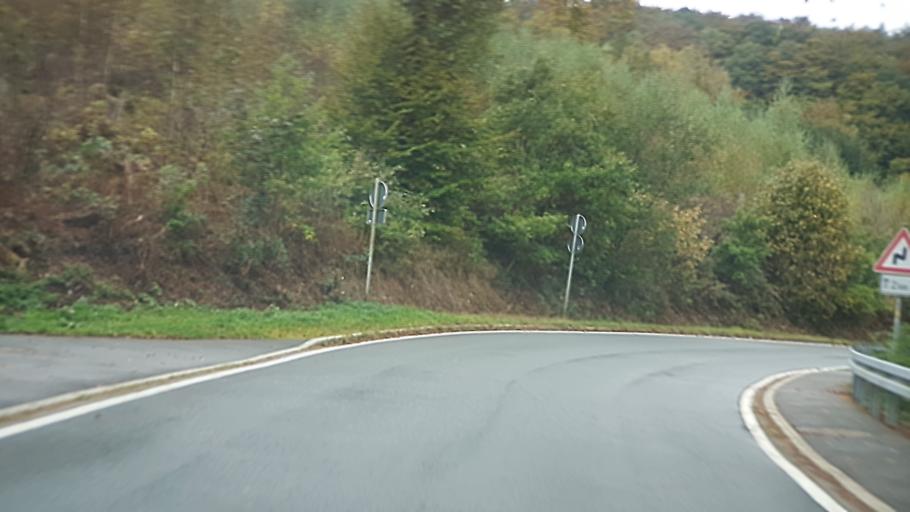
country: DE
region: North Rhine-Westphalia
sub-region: Regierungsbezirk Arnsberg
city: Luedenscheid
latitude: 51.1806
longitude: 7.6719
